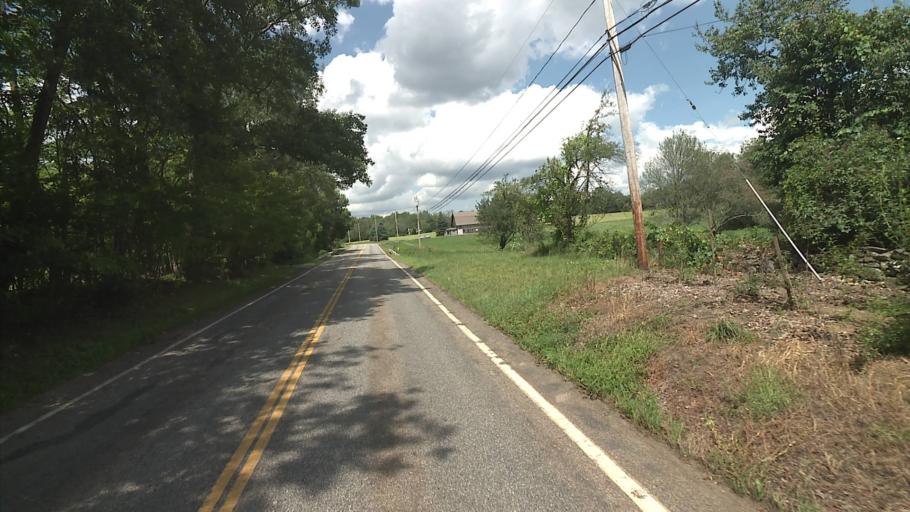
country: US
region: Connecticut
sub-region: Tolland County
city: Stafford Springs
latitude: 41.9212
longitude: -72.1919
